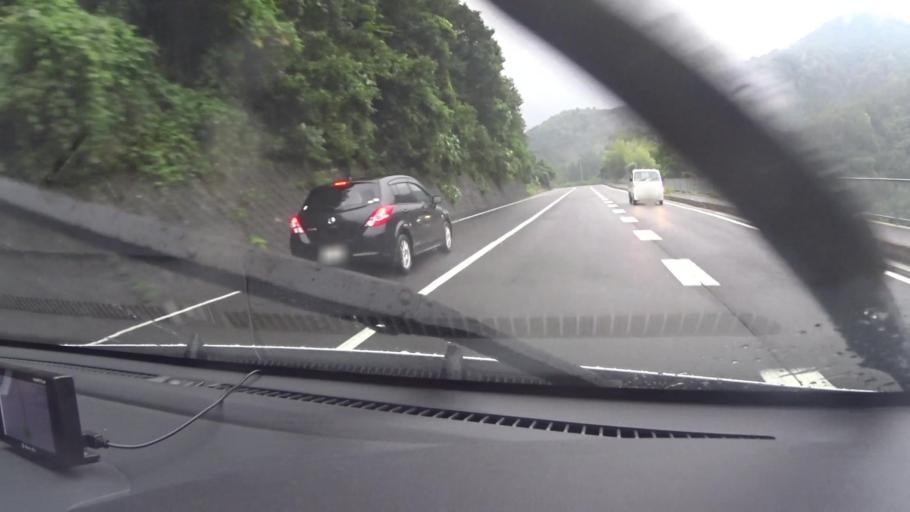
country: JP
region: Kyoto
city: Ayabe
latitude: 35.2631
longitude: 135.2721
